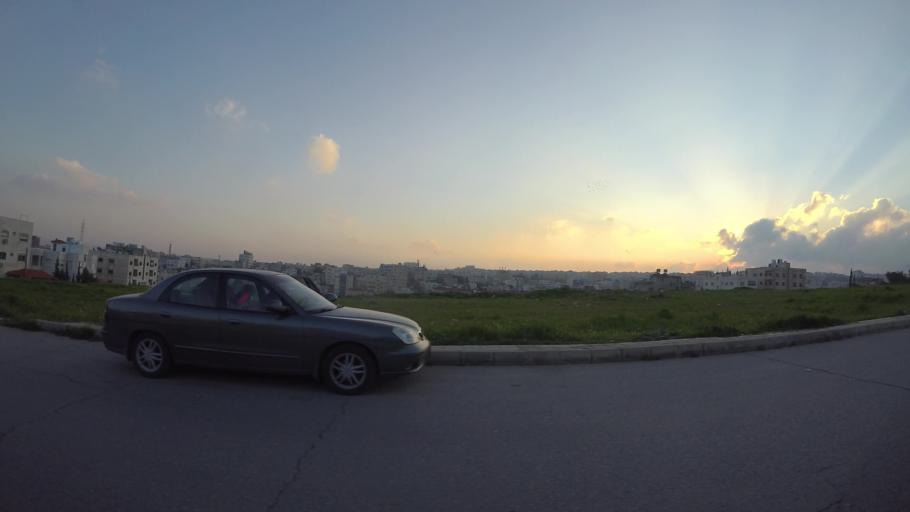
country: JO
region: Amman
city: Amman
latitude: 31.9940
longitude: 35.9490
